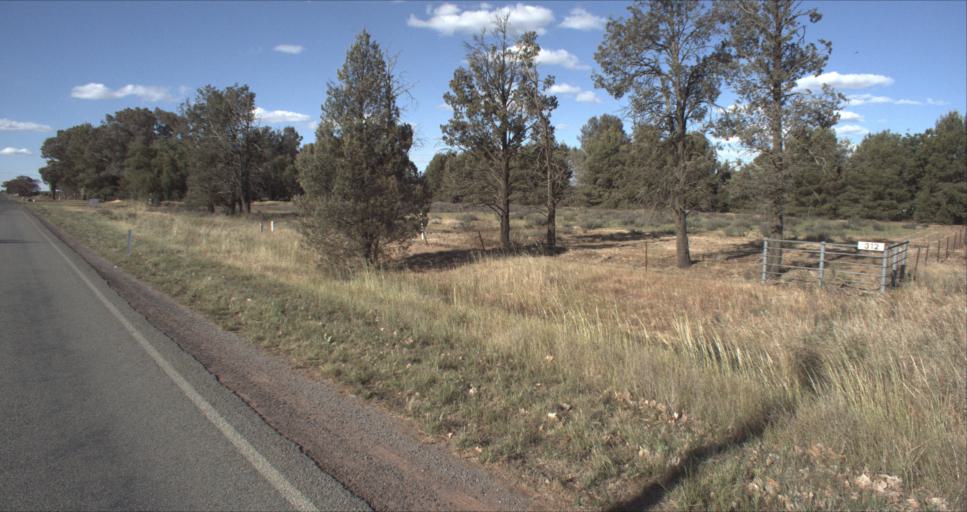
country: AU
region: New South Wales
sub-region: Leeton
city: Leeton
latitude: -34.5262
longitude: 146.2823
